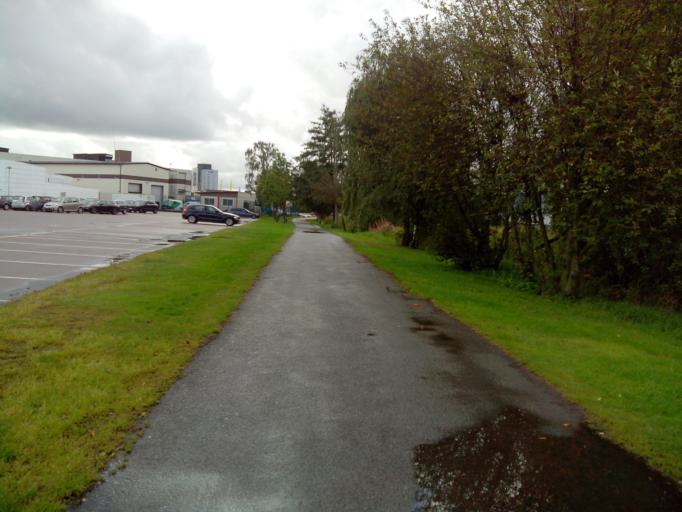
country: SE
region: Vaestra Goetaland
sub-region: Goteborg
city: Goeteborg
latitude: 57.7269
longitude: 11.9512
